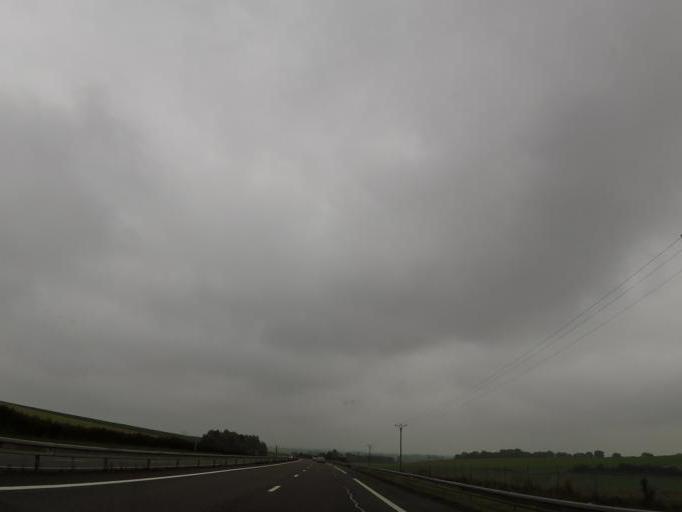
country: FR
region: Champagne-Ardenne
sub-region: Departement de la Marne
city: Sainte-Menehould
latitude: 49.0694
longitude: 4.7597
